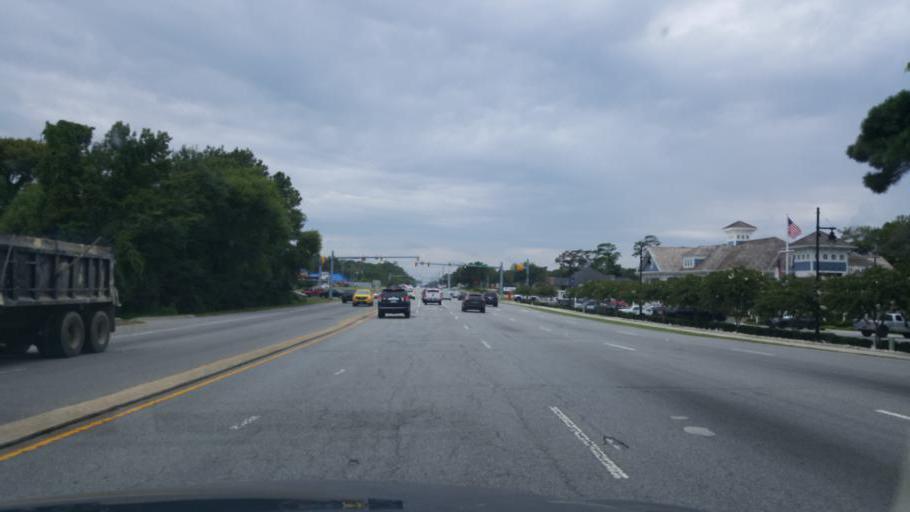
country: US
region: North Carolina
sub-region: Dare County
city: Kitty Hawk
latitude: 36.0994
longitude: -75.7188
